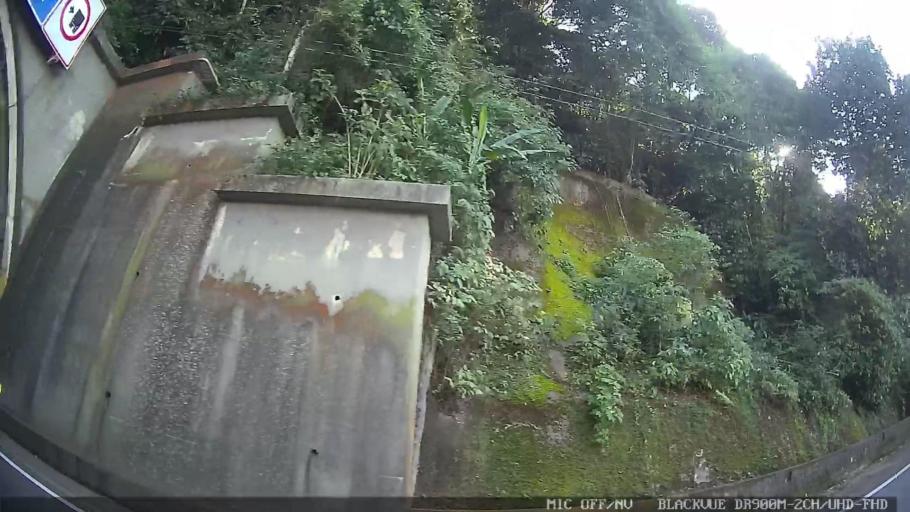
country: BR
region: Sao Paulo
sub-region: Cubatao
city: Cubatao
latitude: -23.8926
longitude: -46.4836
